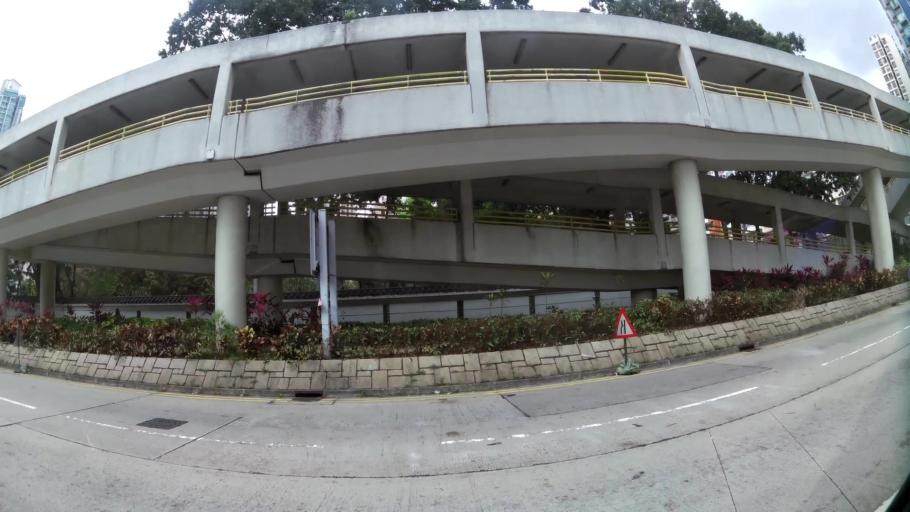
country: HK
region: Wong Tai Sin
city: Wong Tai Sin
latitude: 22.3428
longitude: 114.1986
